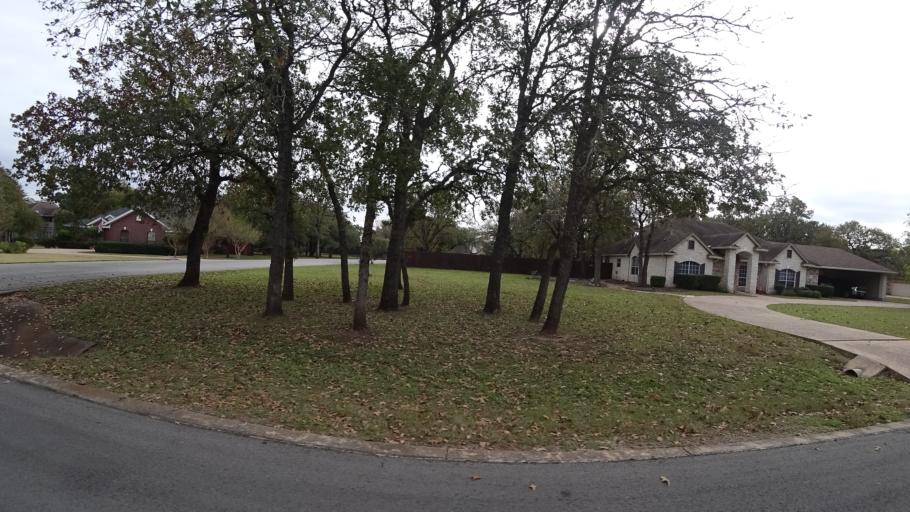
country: US
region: Texas
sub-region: Travis County
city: Shady Hollow
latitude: 30.1428
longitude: -97.8820
